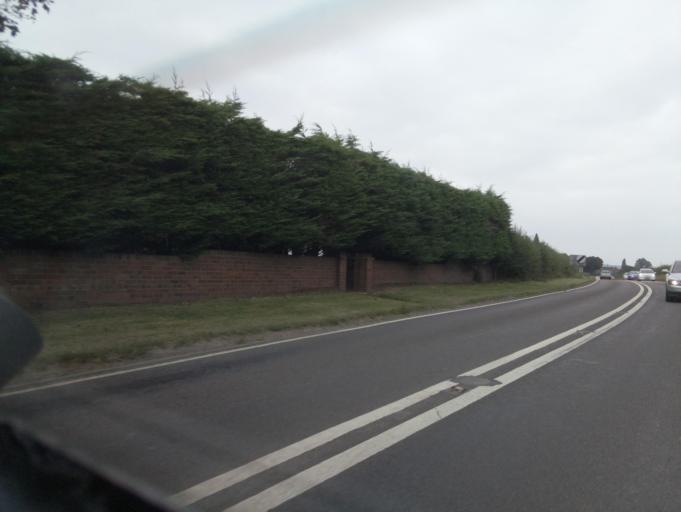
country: GB
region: England
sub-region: Shropshire
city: Shawbury
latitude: 52.7940
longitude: -2.6326
